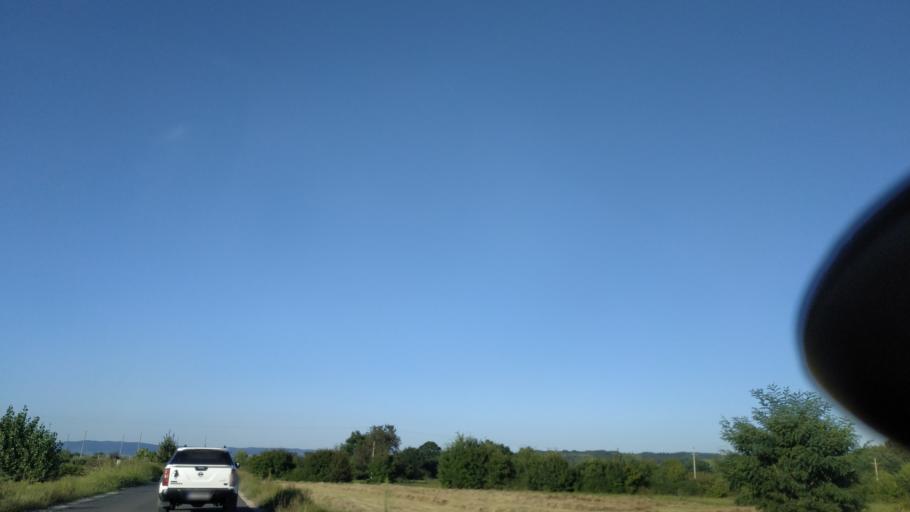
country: RS
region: Central Serbia
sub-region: Rasinski Okrug
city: Krusevac
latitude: 43.5173
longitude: 21.3288
